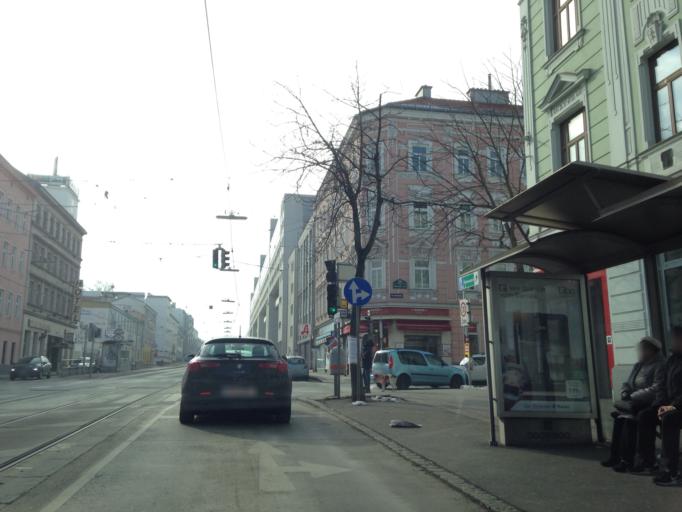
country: AT
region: Vienna
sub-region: Wien Stadt
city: Vienna
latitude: 48.2112
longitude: 16.3057
